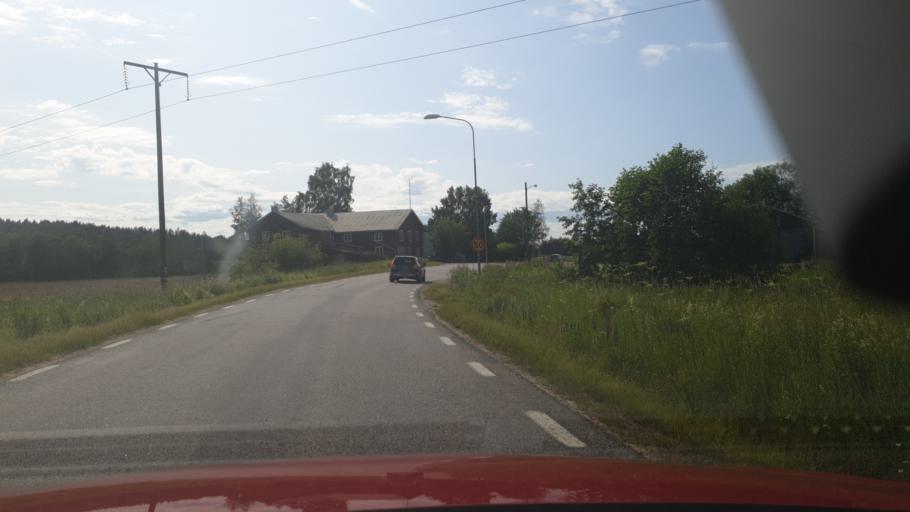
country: SE
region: Gaevleborg
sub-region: Nordanstigs Kommun
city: Bergsjoe
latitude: 62.0426
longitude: 17.2848
